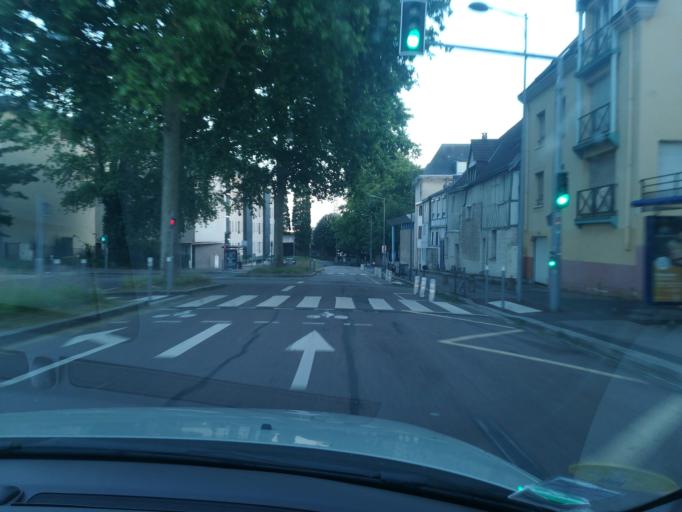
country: FR
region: Haute-Normandie
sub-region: Departement de la Seine-Maritime
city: Rouen
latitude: 49.4448
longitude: 1.1058
